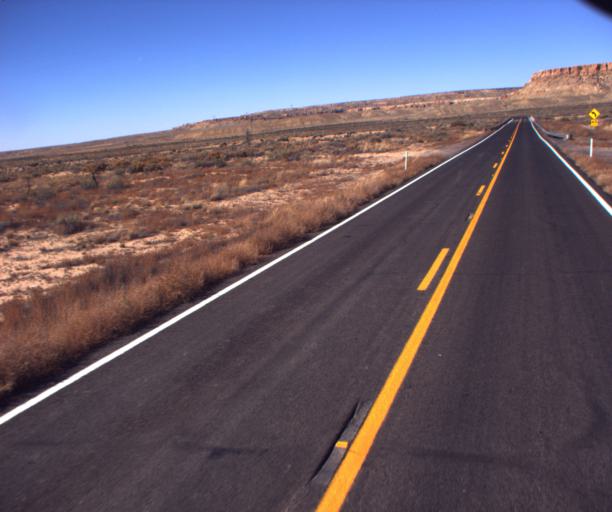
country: US
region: Arizona
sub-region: Navajo County
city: First Mesa
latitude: 35.9815
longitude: -110.7055
